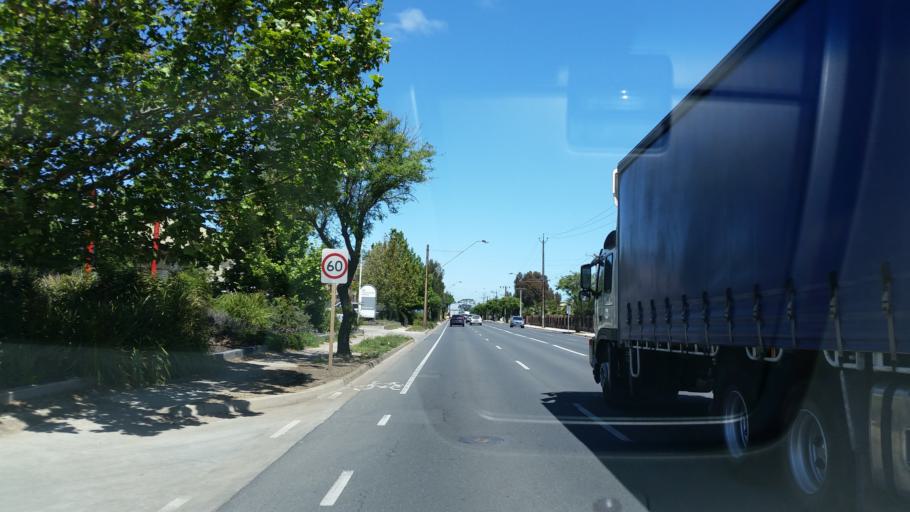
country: AU
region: South Australia
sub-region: Charles Sturt
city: Albert Park
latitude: -34.8712
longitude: 138.5287
